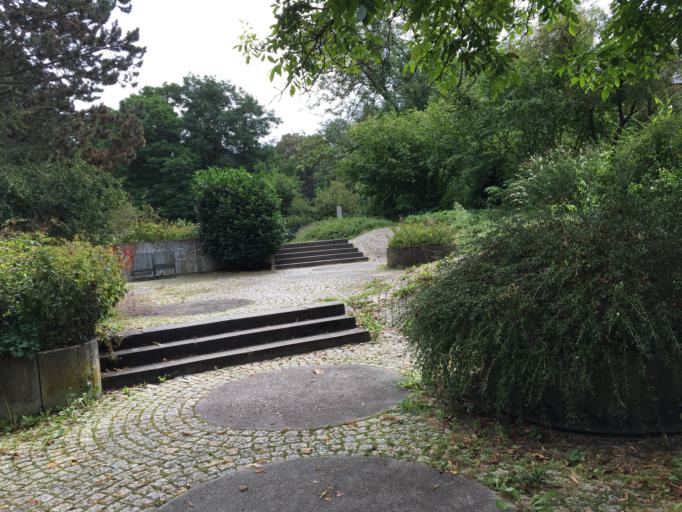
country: DE
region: Hesse
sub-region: Regierungsbezirk Darmstadt
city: Wiesbaden
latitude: 50.0881
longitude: 8.2604
